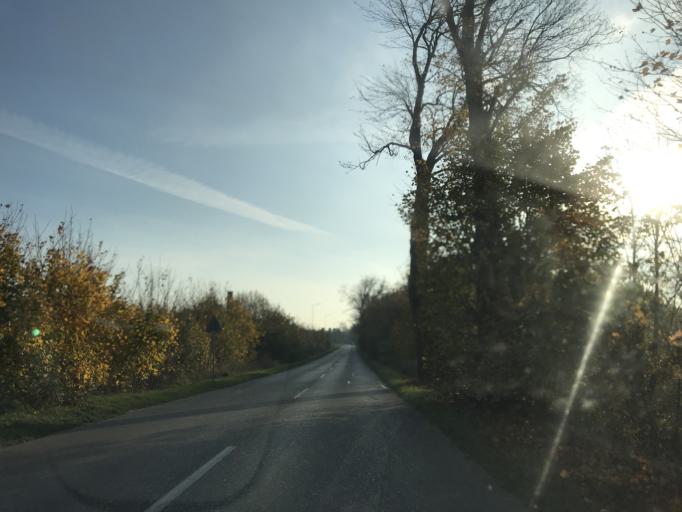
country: PL
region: Pomeranian Voivodeship
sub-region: Powiat pucki
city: Krokowa
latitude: 54.7821
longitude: 18.1536
